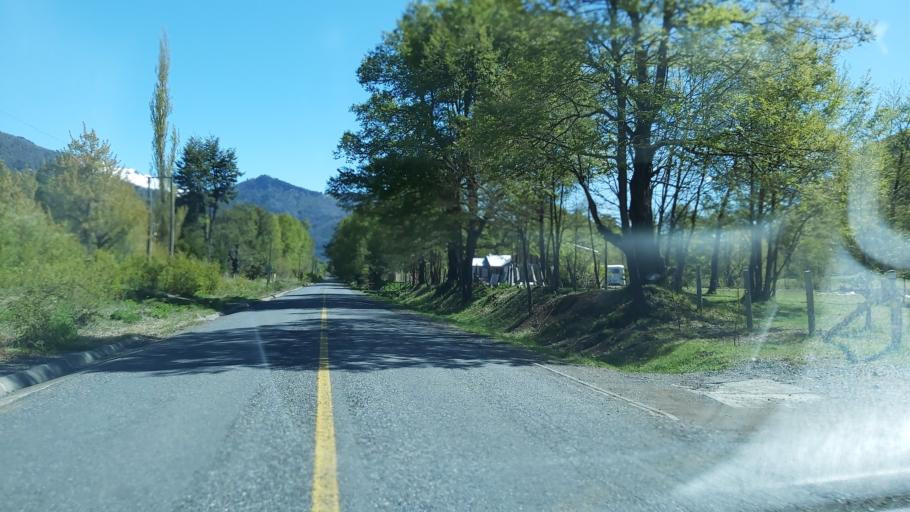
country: CL
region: Araucania
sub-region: Provincia de Cautin
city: Vilcun
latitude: -38.4683
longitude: -71.5219
